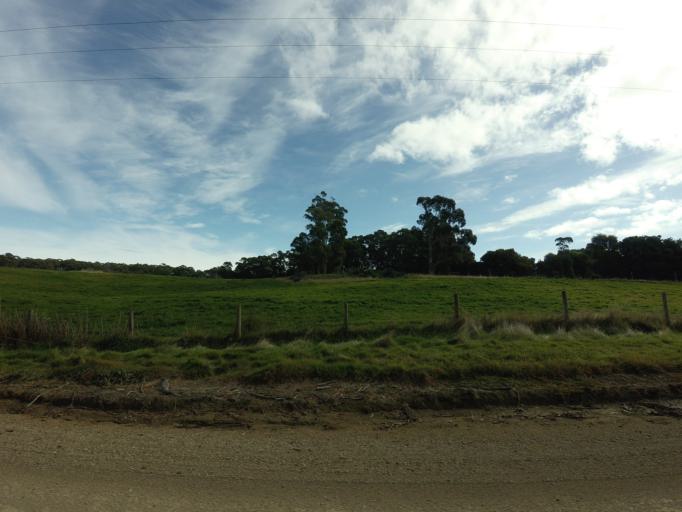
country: AU
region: Tasmania
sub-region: Clarence
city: Sandford
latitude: -43.1647
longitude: 147.7682
